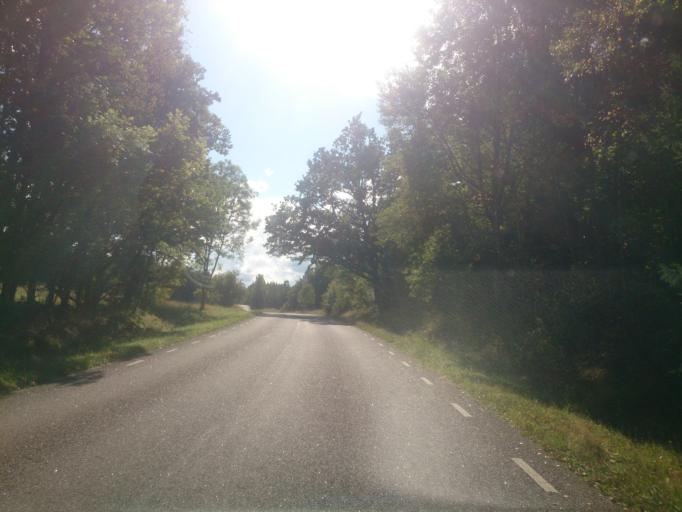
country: SE
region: OEstergoetland
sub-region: Atvidabergs Kommun
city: Atvidaberg
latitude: 58.2633
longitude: 16.0276
